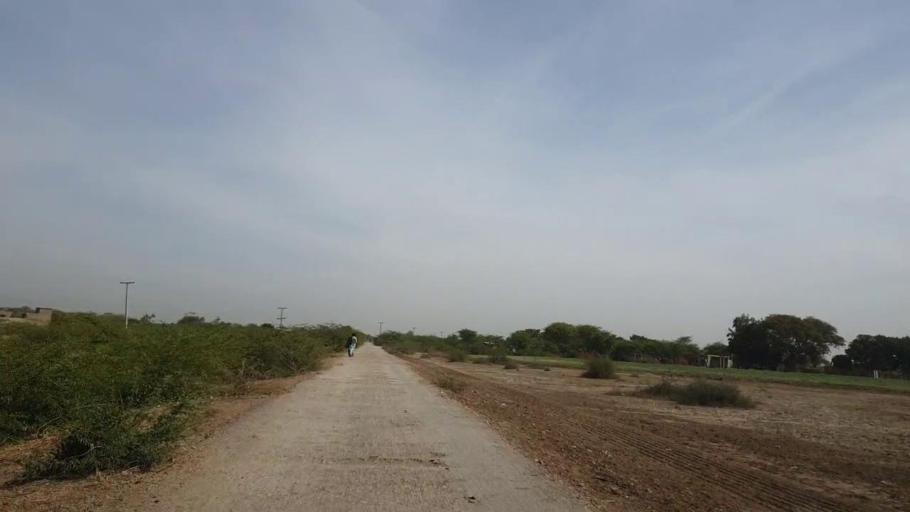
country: PK
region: Sindh
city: Kunri
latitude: 25.1758
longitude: 69.6286
